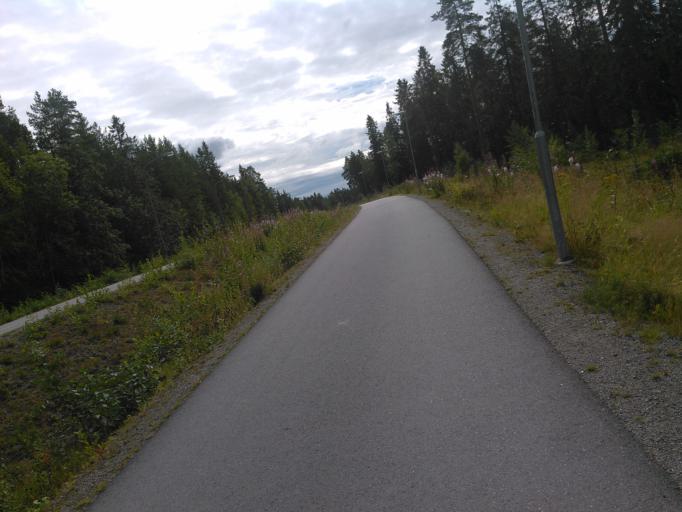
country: SE
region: Vaesterbotten
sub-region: Umea Kommun
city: Umea
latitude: 63.8236
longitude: 20.3137
